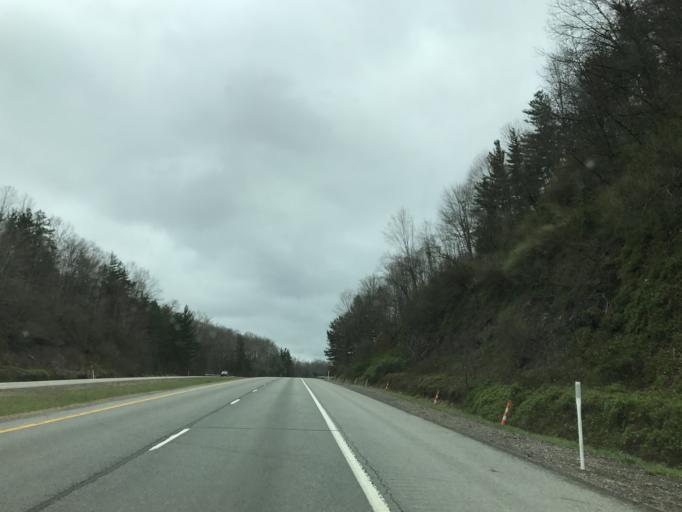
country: US
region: West Virginia
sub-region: Fayette County
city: Mount Hope
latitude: 37.9102
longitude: -81.1689
